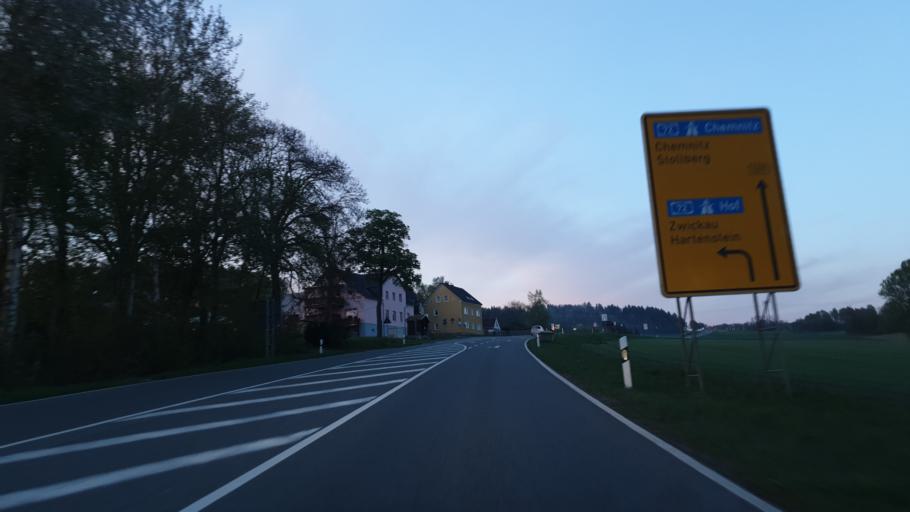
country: DE
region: Saxony
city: Lossnitz
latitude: 50.6393
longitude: 12.7348
